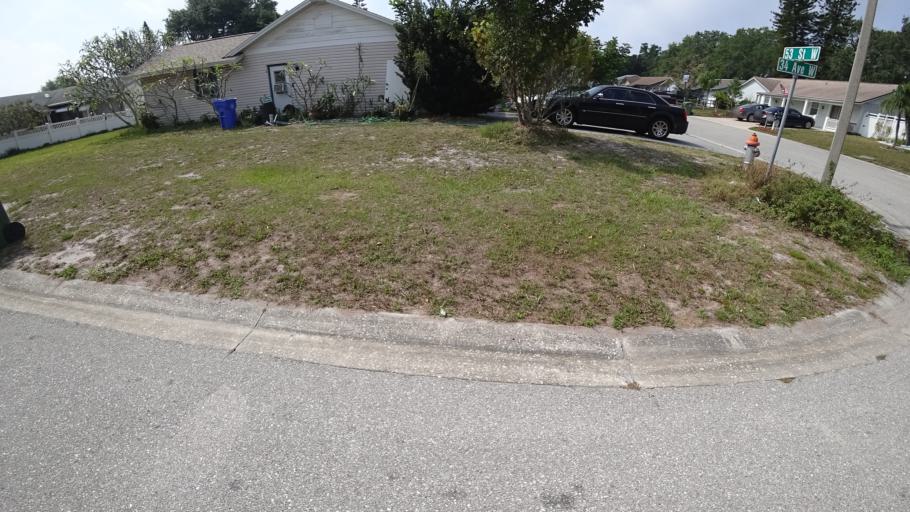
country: US
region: Florida
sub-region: Manatee County
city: West Bradenton
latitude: 27.4713
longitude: -82.6139
